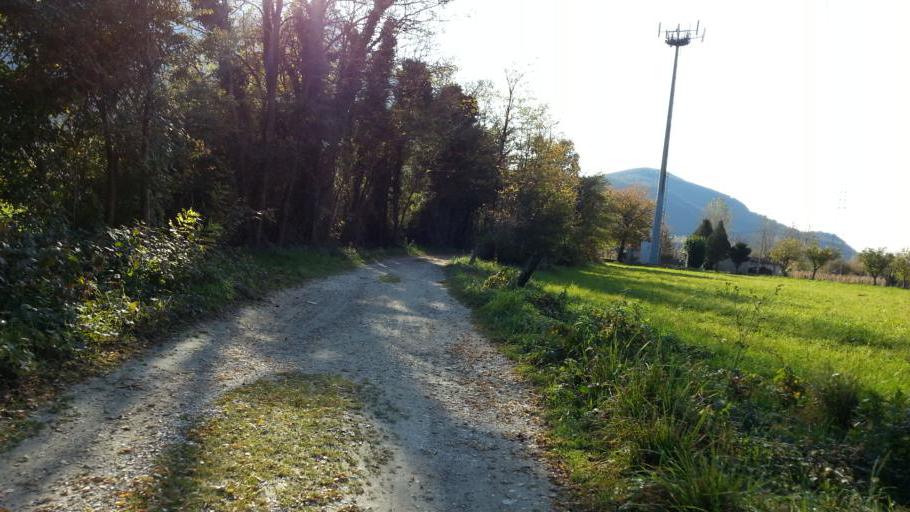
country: IT
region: Friuli Venezia Giulia
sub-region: Provincia di Udine
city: Venzone
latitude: 46.3304
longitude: 13.1323
